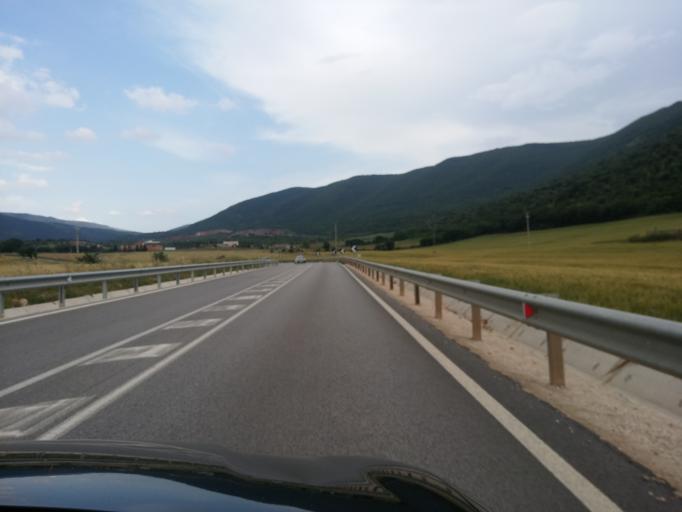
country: IT
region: Apulia
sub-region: Provincia di Foggia
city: Rignano Garganico
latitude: 41.7143
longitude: 15.5320
